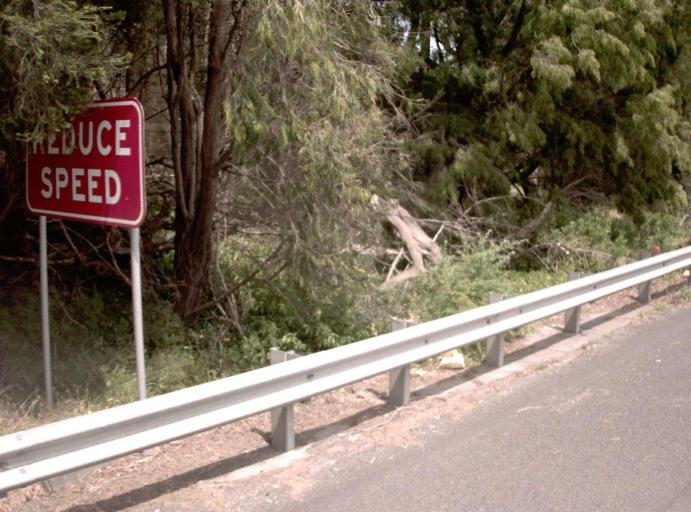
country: AU
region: Victoria
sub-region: Frankston
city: Frankston East
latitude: -38.1410
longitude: 145.1367
